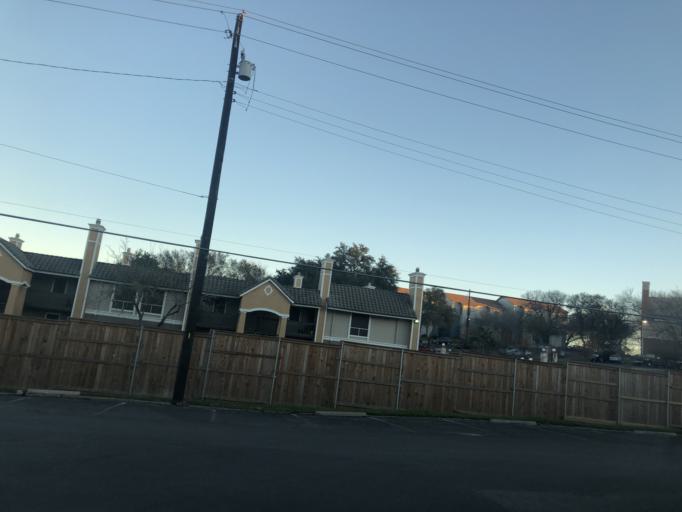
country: US
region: Texas
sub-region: Travis County
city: Austin
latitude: 30.2327
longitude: -97.7304
